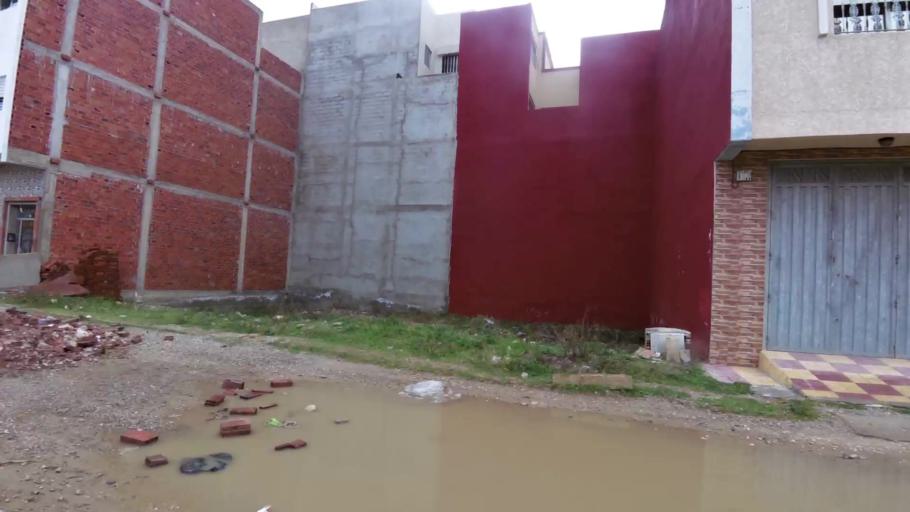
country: MA
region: Tanger-Tetouan
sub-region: Tetouan
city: Martil
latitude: 35.6144
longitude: -5.3032
